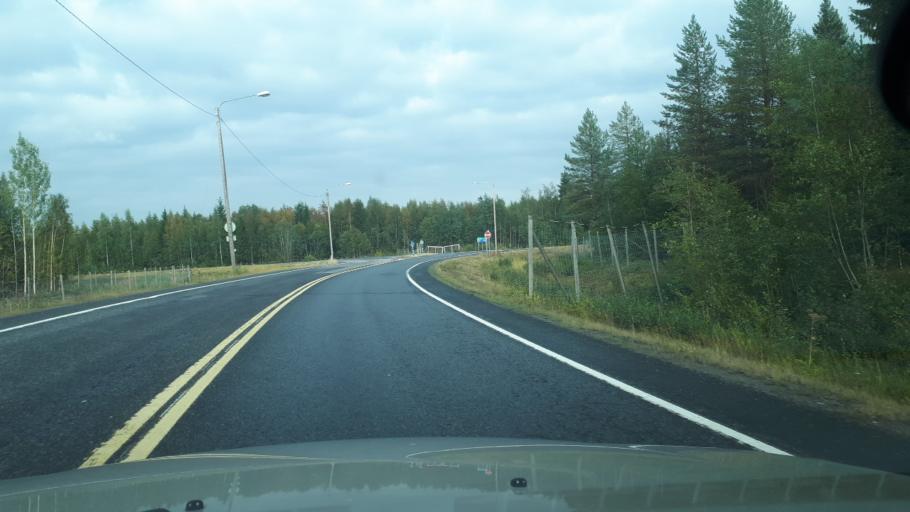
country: FI
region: Northern Ostrobothnia
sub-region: Oulunkaari
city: Ii
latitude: 65.2643
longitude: 25.3614
